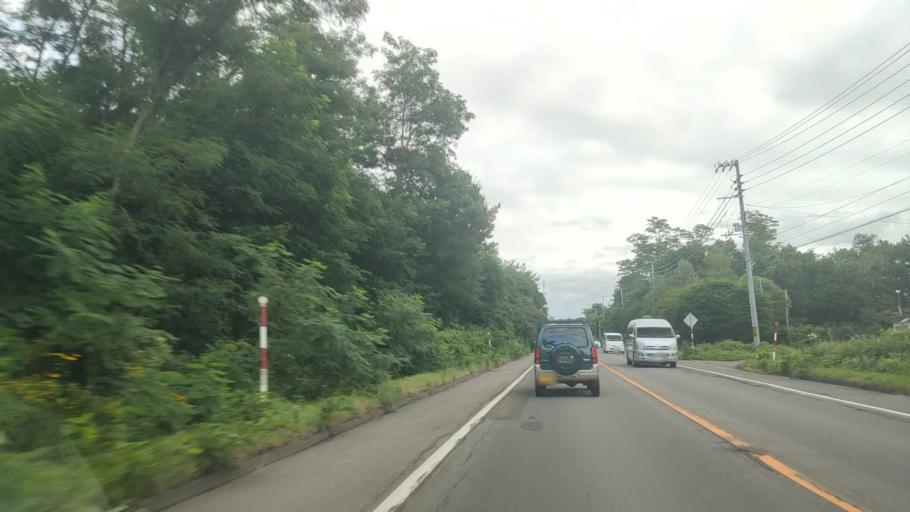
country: JP
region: Hokkaido
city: Nanae
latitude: 42.0707
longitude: 140.6031
